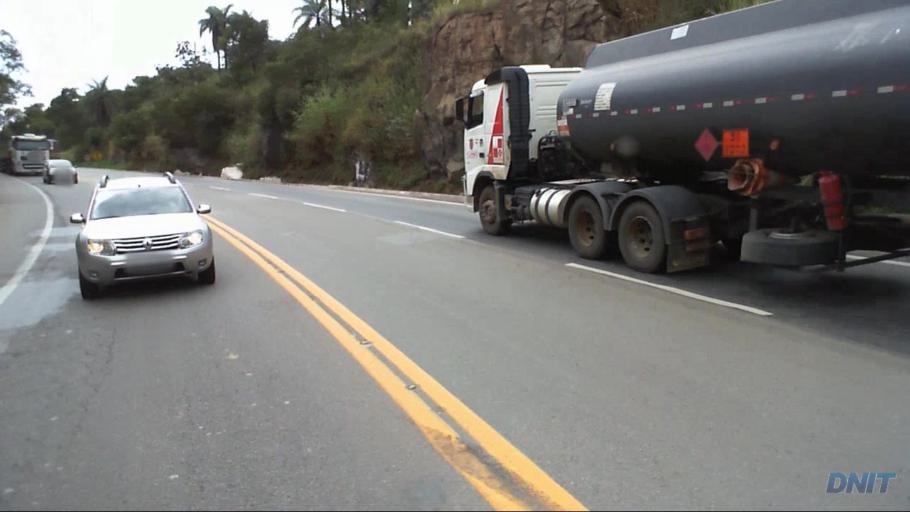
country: BR
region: Minas Gerais
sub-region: Caete
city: Caete
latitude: -19.7850
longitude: -43.6613
